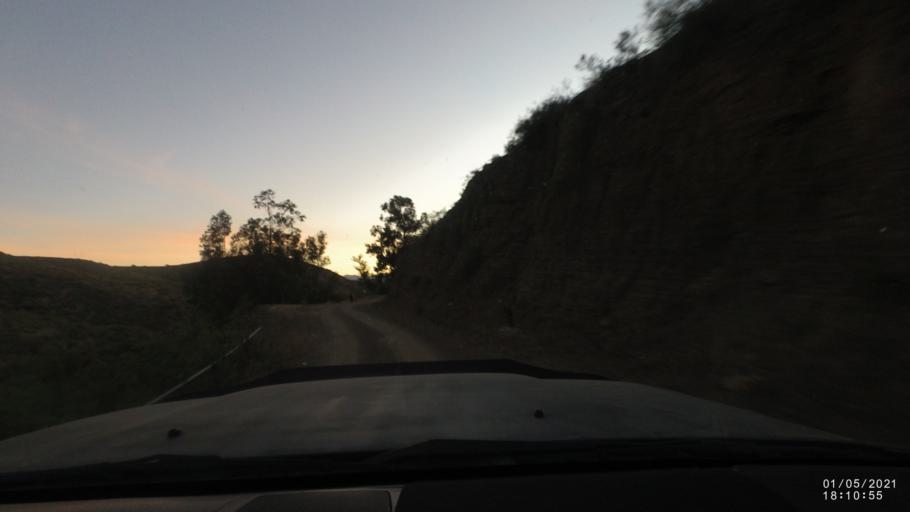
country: BO
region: Cochabamba
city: Capinota
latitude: -17.6842
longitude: -66.1976
